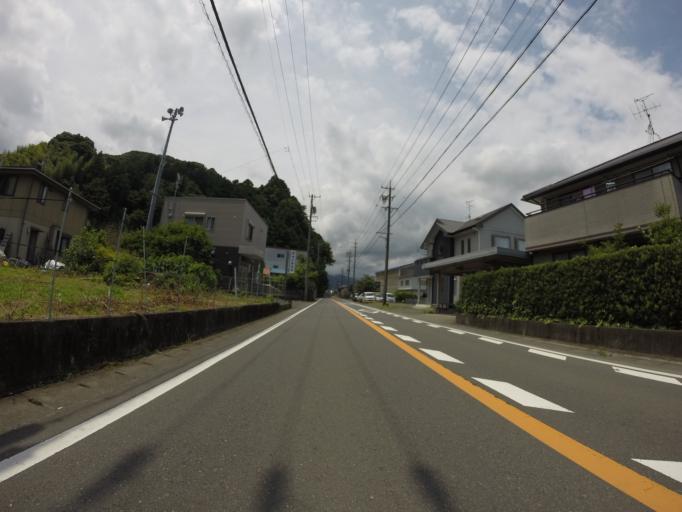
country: JP
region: Shizuoka
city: Shizuoka-shi
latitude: 34.9783
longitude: 138.3300
